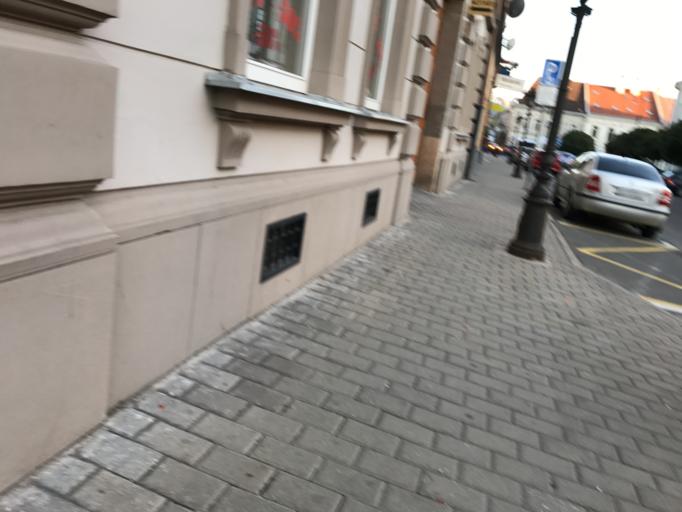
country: SK
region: Kosicky
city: Kosice
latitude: 48.7215
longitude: 21.2554
